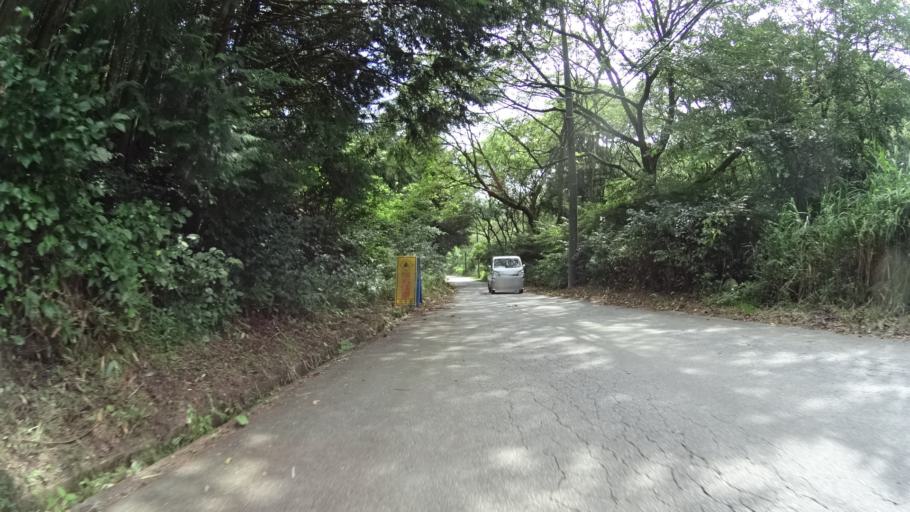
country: JP
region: Yamanashi
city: Nirasaki
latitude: 35.7814
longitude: 138.5346
